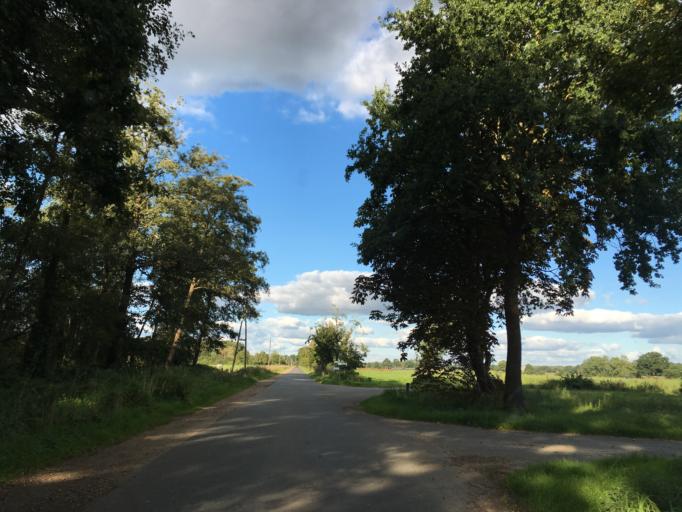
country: DE
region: Lower Saxony
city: Salzhausen
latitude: 53.2338
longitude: 10.1755
